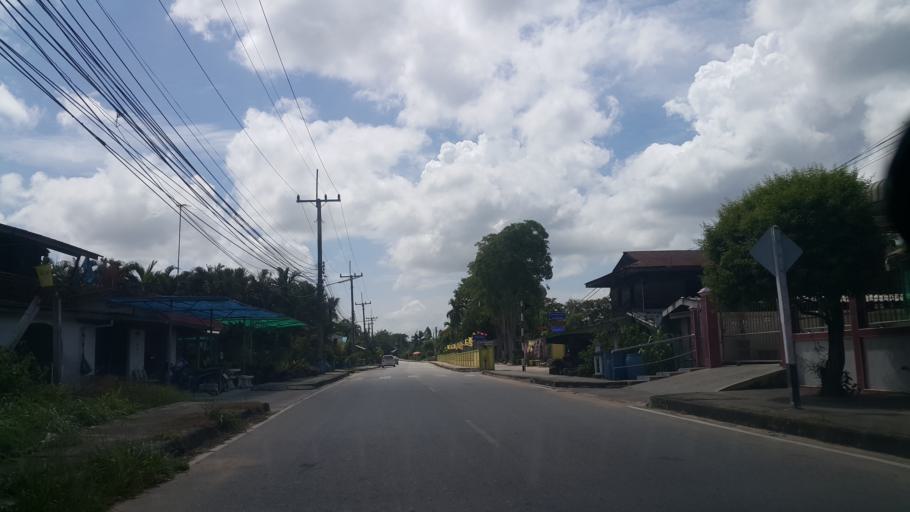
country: TH
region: Rayong
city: Ban Chang
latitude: 12.7950
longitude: 101.0293
